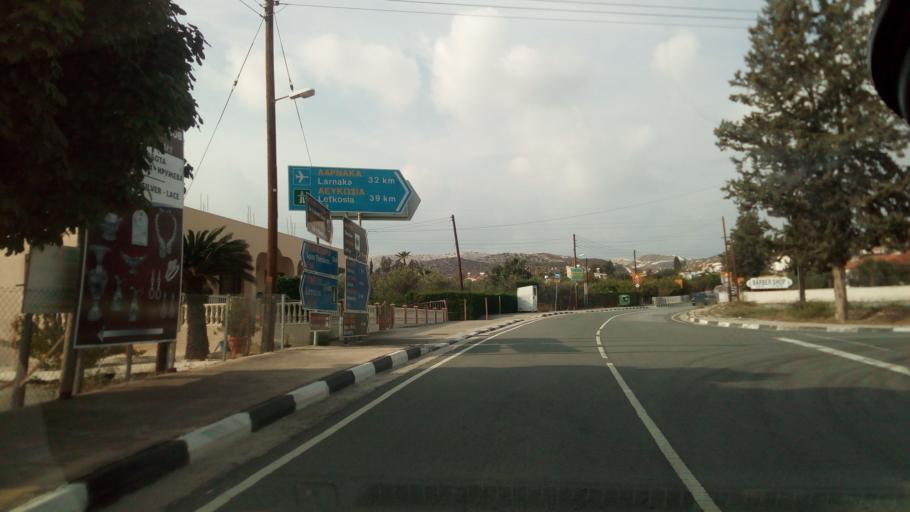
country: CY
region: Larnaka
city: Kofinou
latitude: 34.8174
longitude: 33.3598
